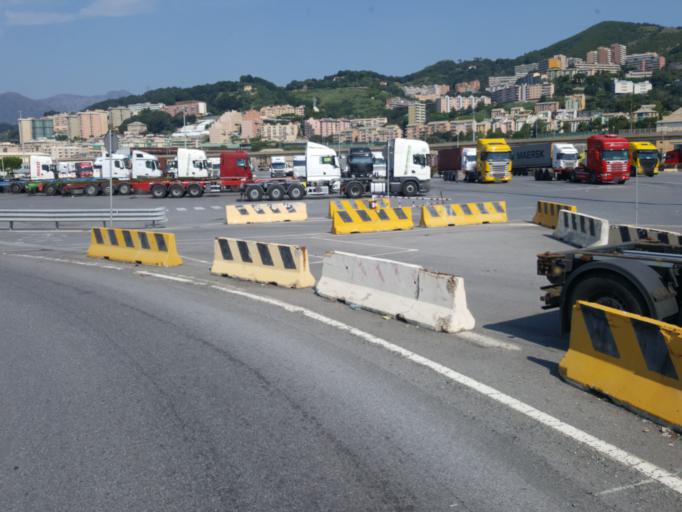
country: IT
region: Liguria
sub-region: Provincia di Genova
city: Mele
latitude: 44.4246
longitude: 8.7693
